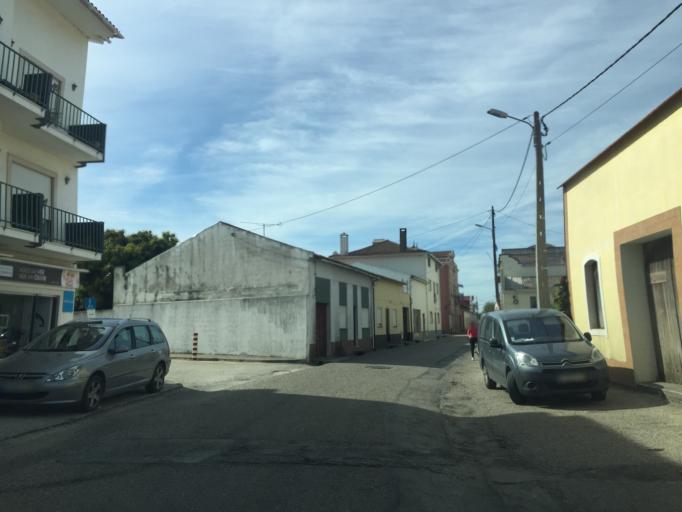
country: PT
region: Coimbra
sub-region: Figueira da Foz
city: Lavos
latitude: 40.0709
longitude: -8.8050
